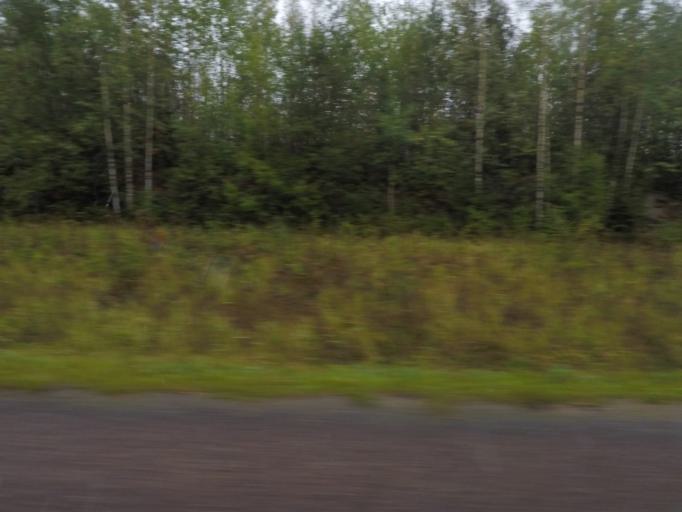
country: FI
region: Northern Savo
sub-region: Varkaus
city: Leppaevirta
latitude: 62.4475
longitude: 27.7944
